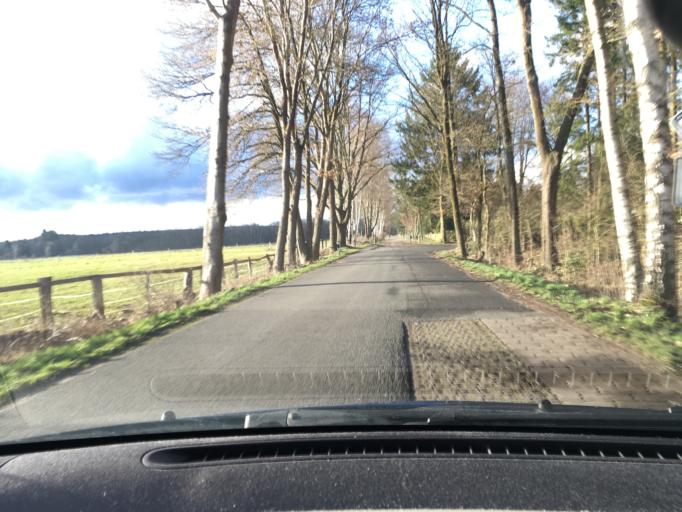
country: DE
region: Lower Saxony
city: Jesteburg
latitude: 53.3080
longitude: 9.9849
